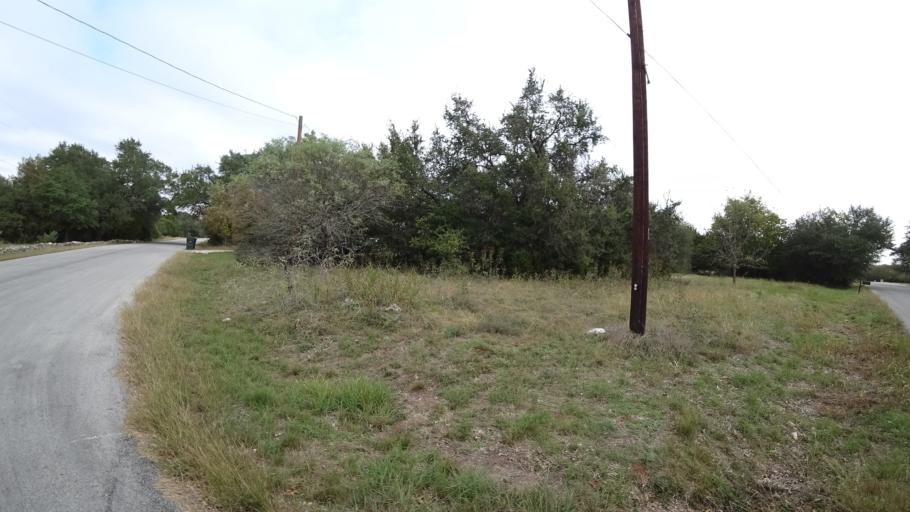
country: US
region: Texas
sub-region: Travis County
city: Shady Hollow
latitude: 30.1455
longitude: -97.8807
